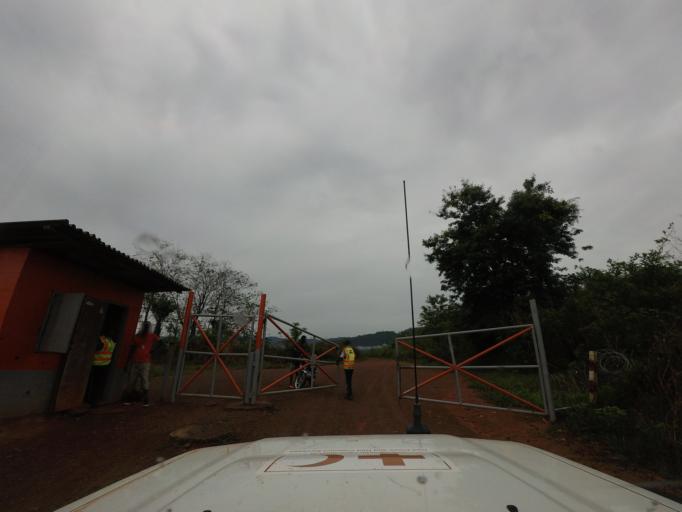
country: LR
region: Nimba
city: New Yekepa
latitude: 7.5684
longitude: -8.5579
